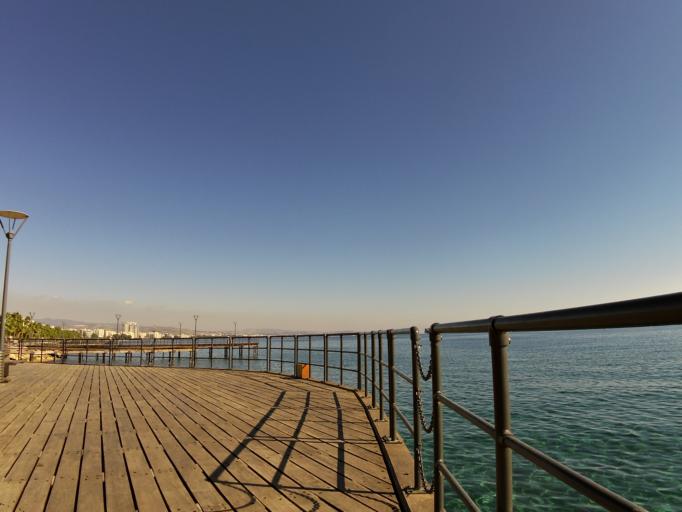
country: CY
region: Limassol
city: Limassol
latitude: 34.6735
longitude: 33.0469
